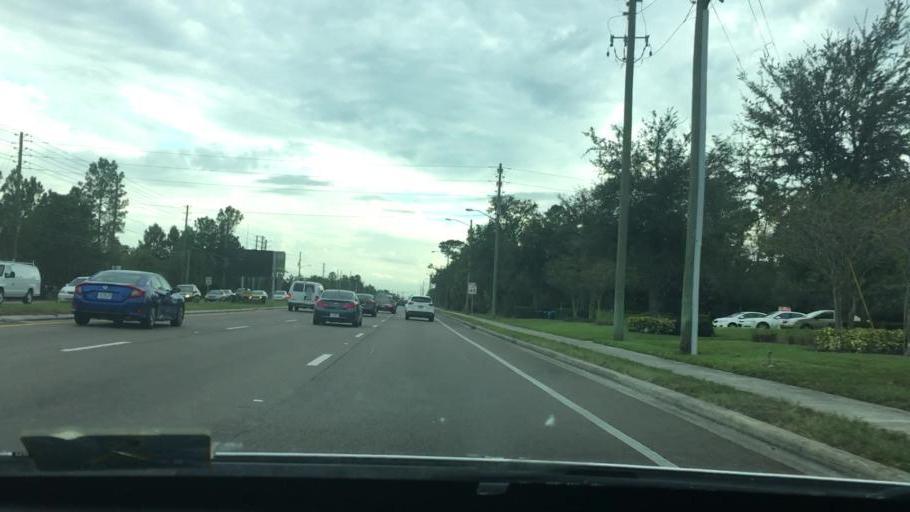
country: US
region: Florida
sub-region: Orange County
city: Alafaya
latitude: 28.6064
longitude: -81.2077
